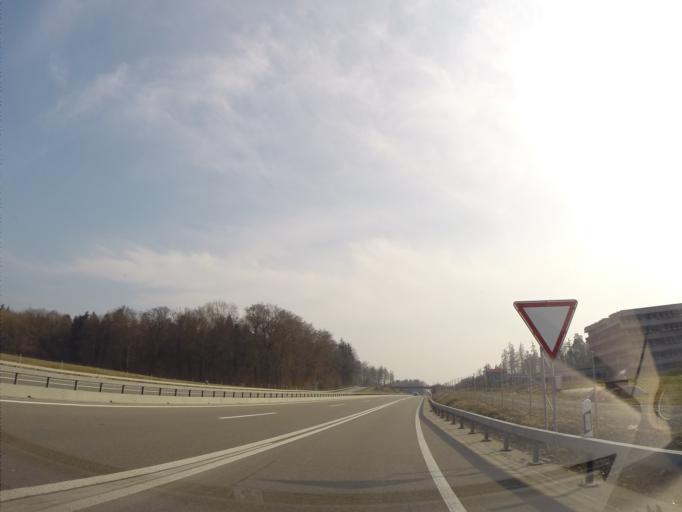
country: CH
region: Zurich
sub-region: Bezirk Andelfingen
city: Kleinandelfingen
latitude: 47.6192
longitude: 8.6832
